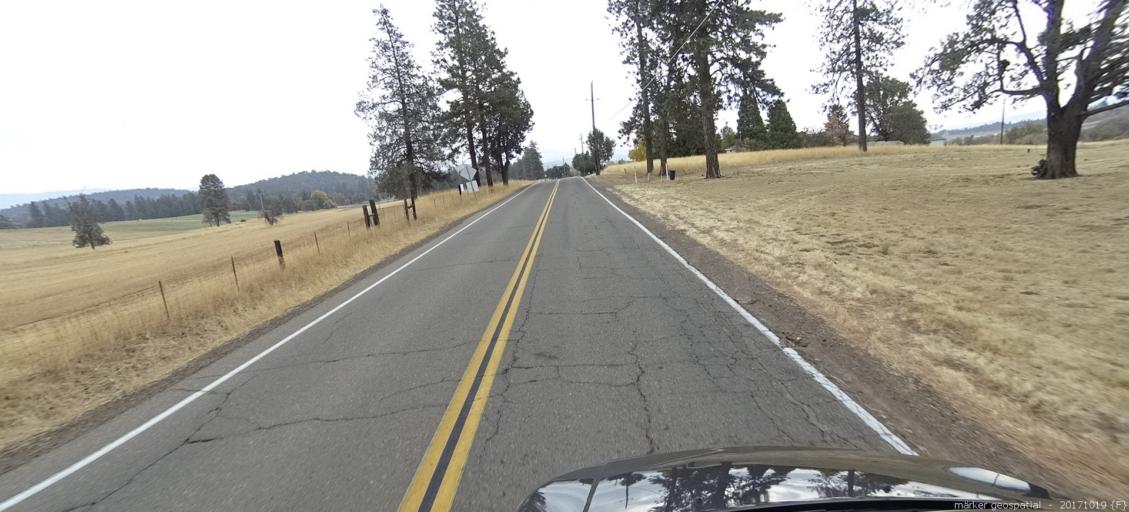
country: US
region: California
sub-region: Shasta County
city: Burney
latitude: 41.0515
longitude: -121.3483
